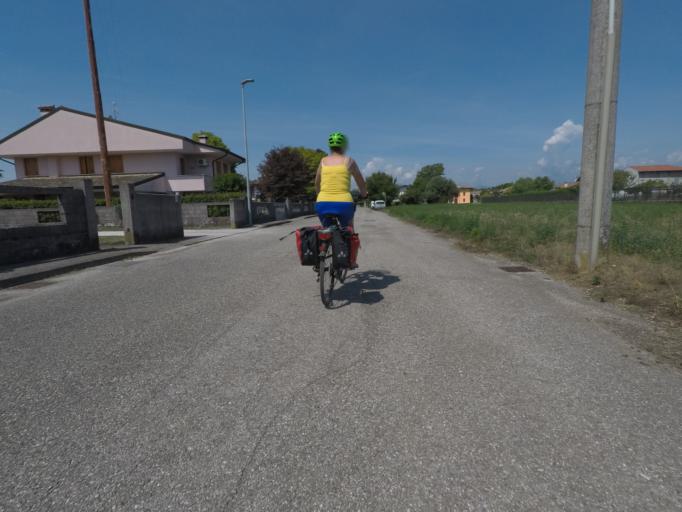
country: IT
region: Friuli Venezia Giulia
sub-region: Provincia di Udine
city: Dignano
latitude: 46.0844
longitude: 12.9452
